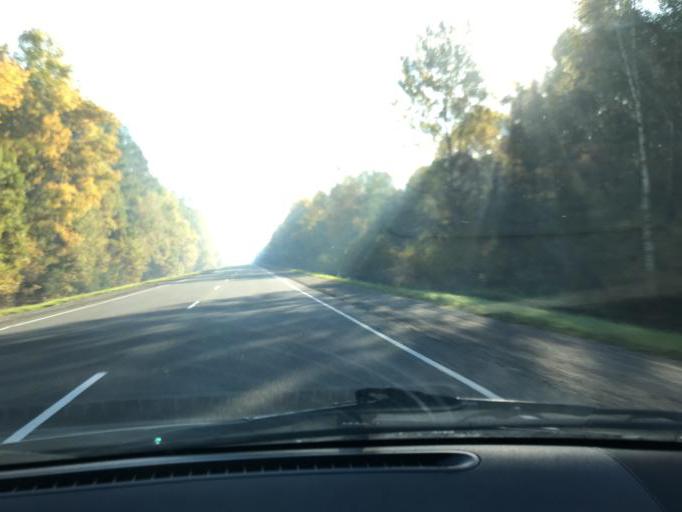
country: BY
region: Brest
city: Horad Luninyets
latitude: 52.2959
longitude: 26.7466
